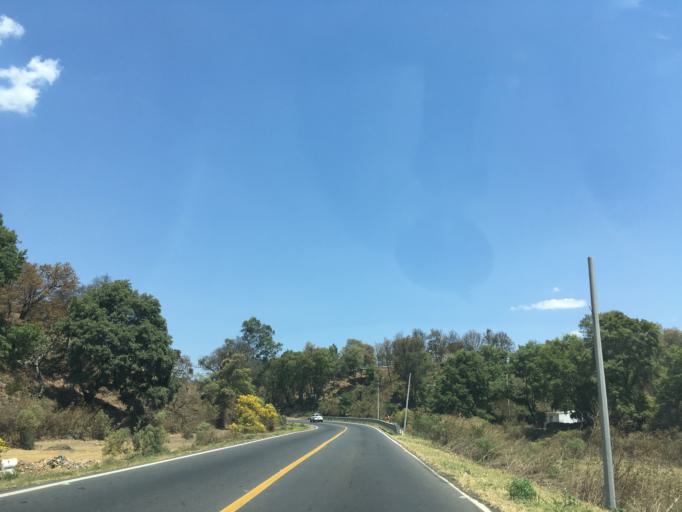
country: MX
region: Michoacan
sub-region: Chilchota
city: Tacuro (Santa Maria Tacuro)
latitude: 19.8427
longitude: -102.0313
